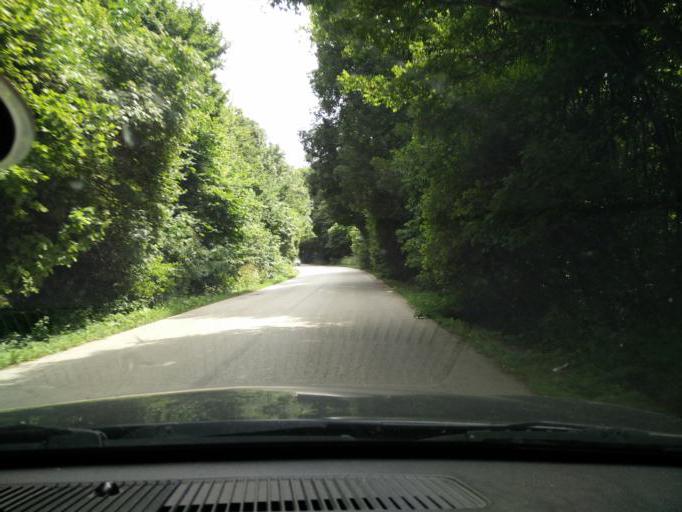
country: HU
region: Komarom-Esztergom
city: Tardos
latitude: 47.6574
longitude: 18.4219
